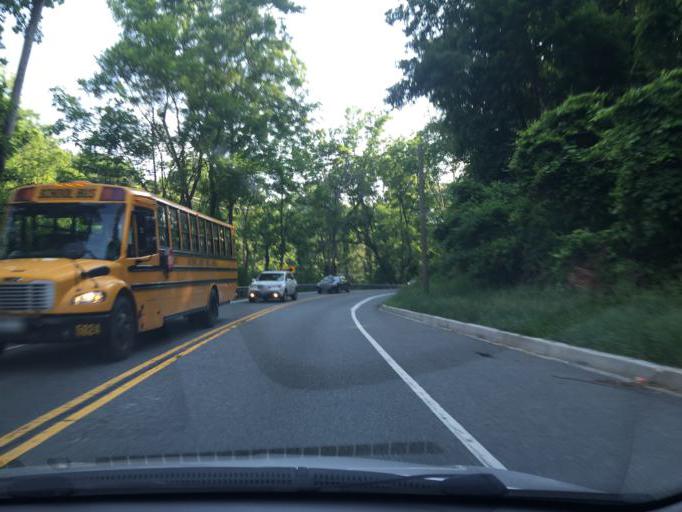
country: US
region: Maryland
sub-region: Baltimore County
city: Hunt Valley
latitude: 39.5051
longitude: -76.6488
